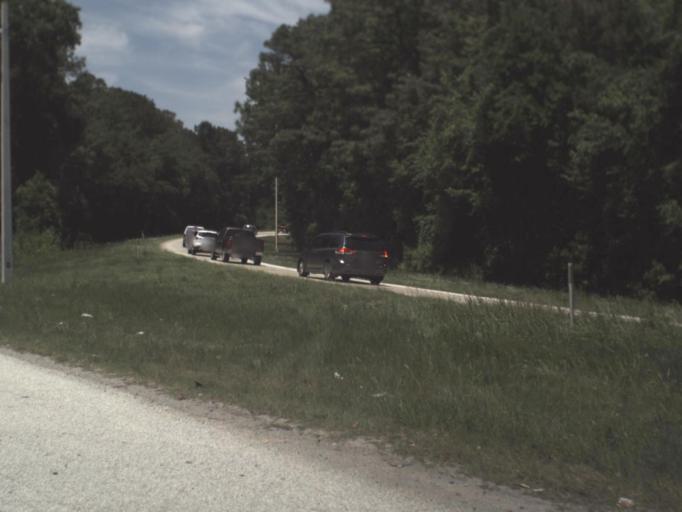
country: US
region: Florida
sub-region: Duval County
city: Jacksonville
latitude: 30.4592
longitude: -81.6445
